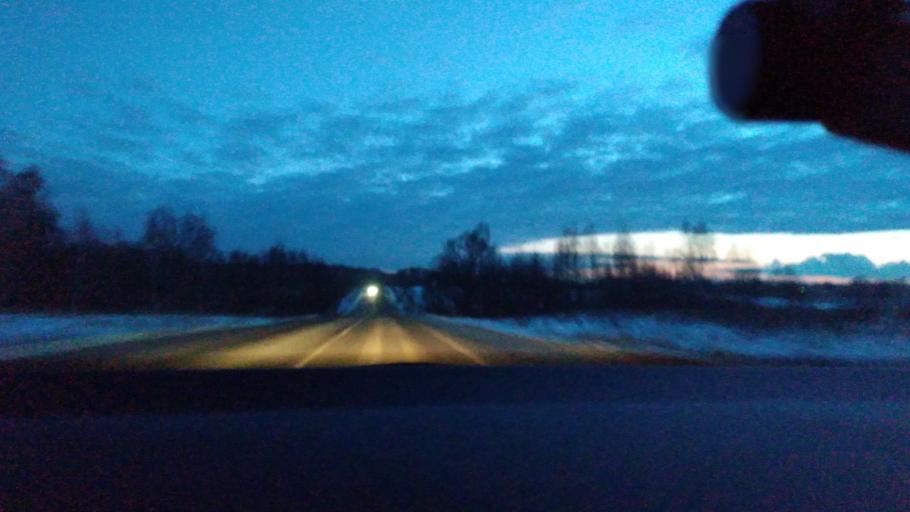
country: RU
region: Moskovskaya
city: Krasnaya Poyma
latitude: 55.1598
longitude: 39.2218
